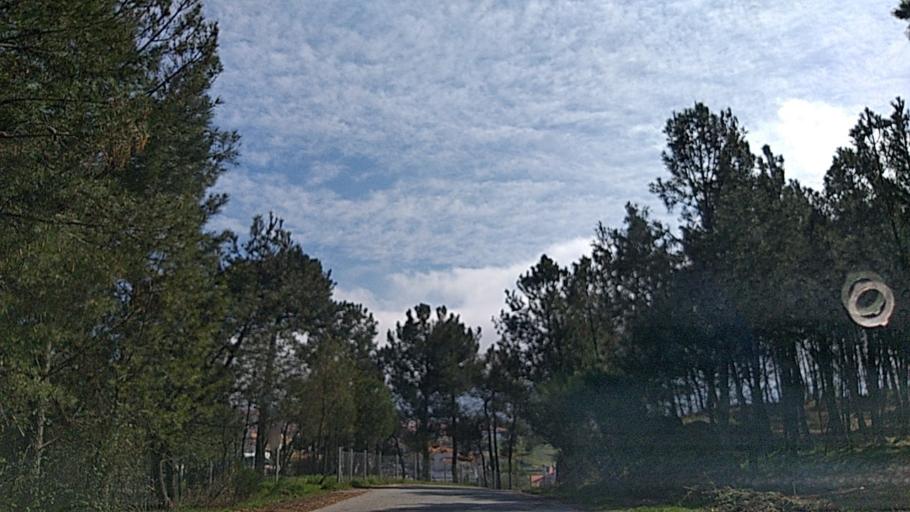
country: PT
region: Guarda
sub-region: Celorico da Beira
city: Celorico da Beira
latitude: 40.6326
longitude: -7.4032
